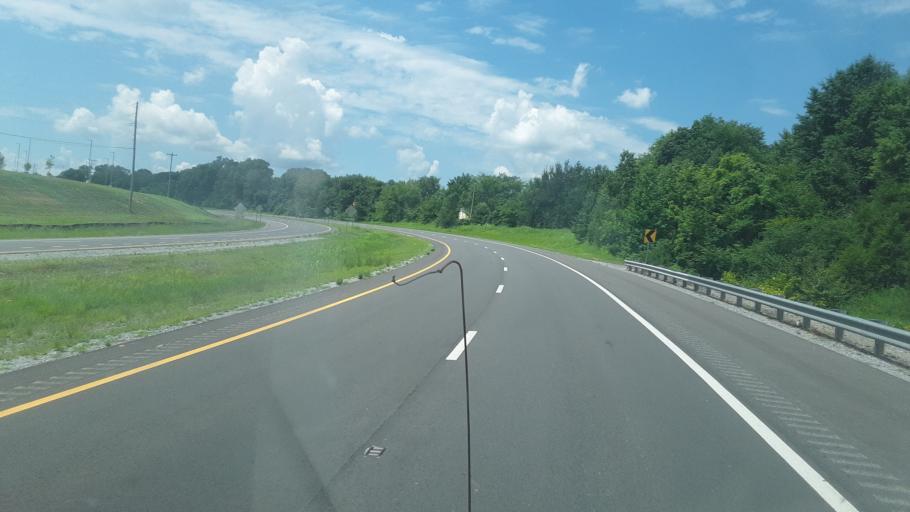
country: US
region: Kentucky
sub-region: Christian County
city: Fort Campbell North
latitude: 36.5821
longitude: -87.4425
